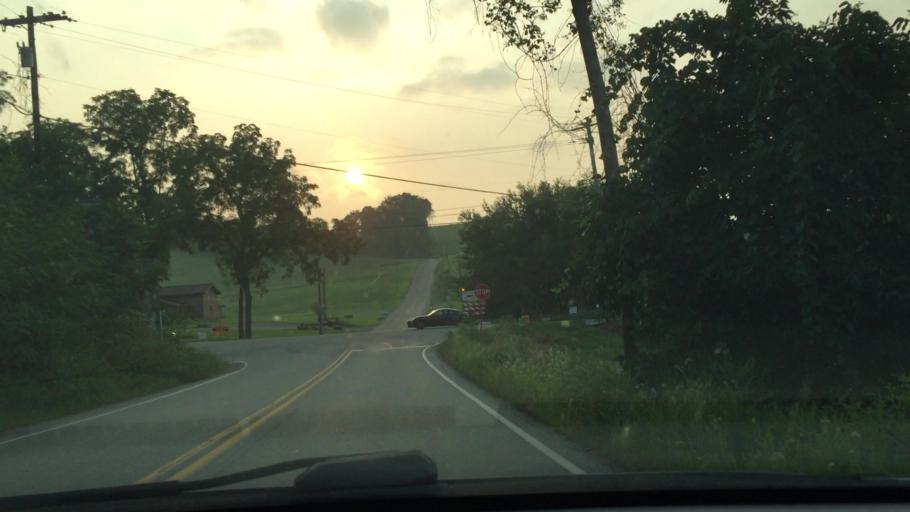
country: US
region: Pennsylvania
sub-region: Westmoreland County
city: Fellsburg
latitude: 40.1682
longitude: -79.8174
